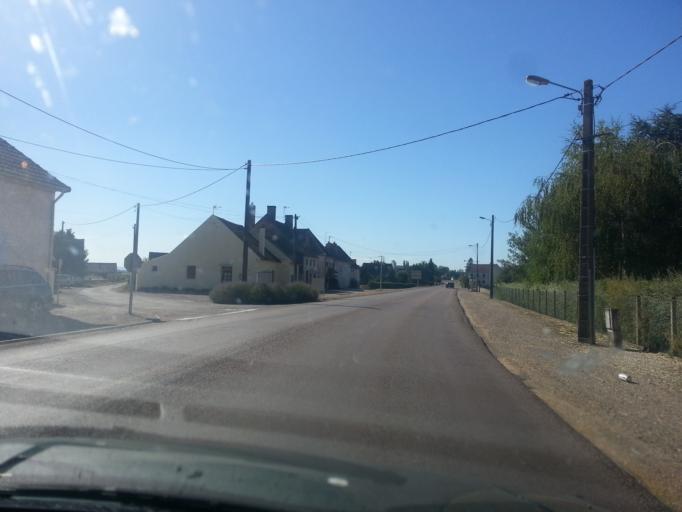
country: FR
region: Bourgogne
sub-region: Departement de Saone-et-Loire
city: Verdun-sur-le-Doubs
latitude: 46.8844
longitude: 5.0413
